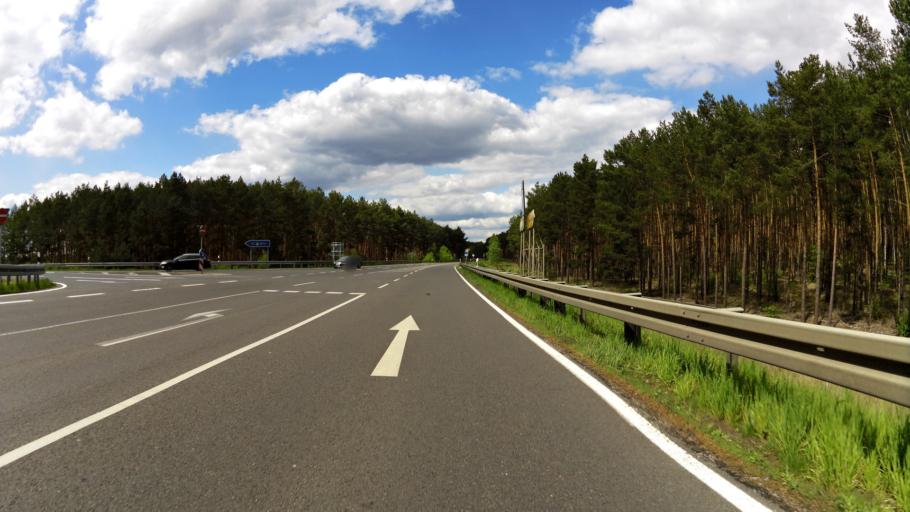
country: DE
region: Brandenburg
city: Langewahl
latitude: 52.3366
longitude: 14.1095
